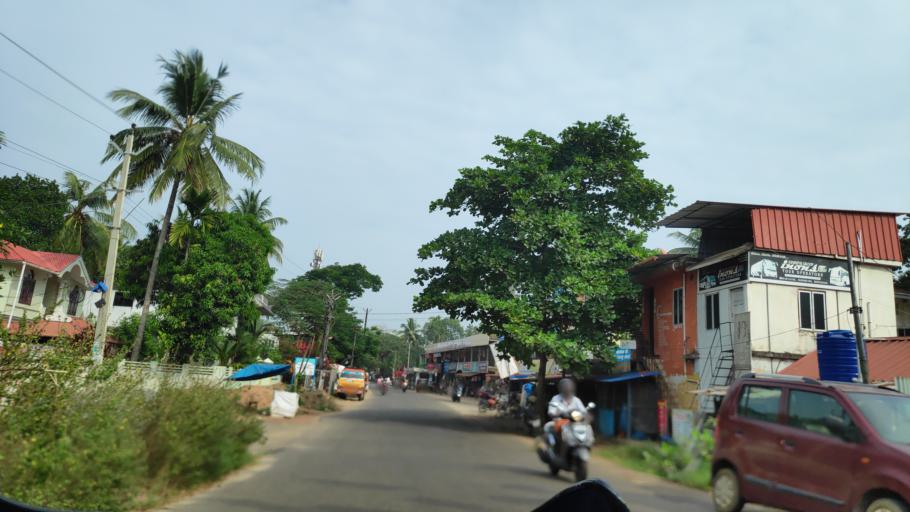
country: IN
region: Kerala
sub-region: Alappuzha
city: Kutiatodu
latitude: 9.7966
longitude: 76.3542
